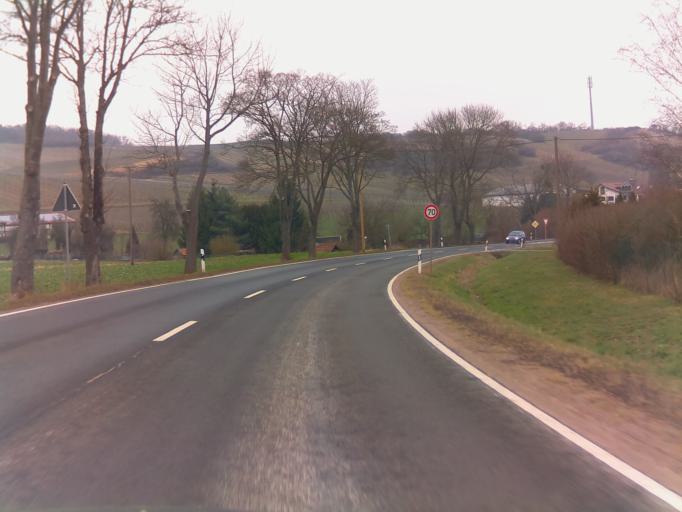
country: DE
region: Rheinland-Pfalz
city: Frei-Laubersheim
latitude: 49.8013
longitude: 7.8955
